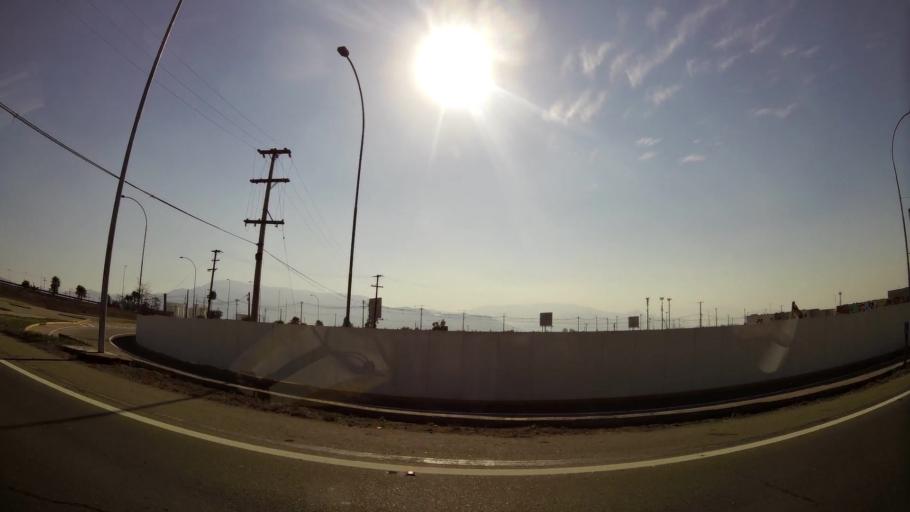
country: CL
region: Santiago Metropolitan
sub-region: Provincia de Santiago
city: Lo Prado
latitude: -33.4097
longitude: -70.7921
